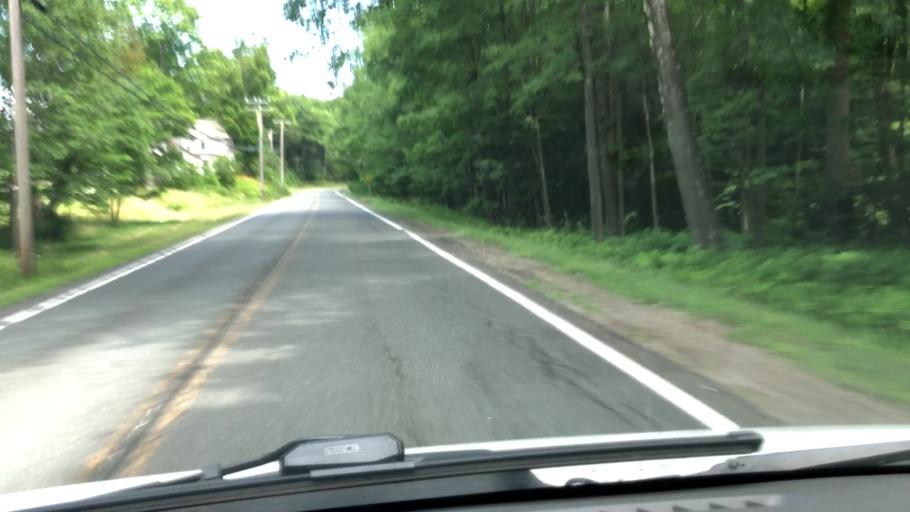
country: US
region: Massachusetts
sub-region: Hampshire County
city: Williamsburg
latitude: 42.4264
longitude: -72.7833
